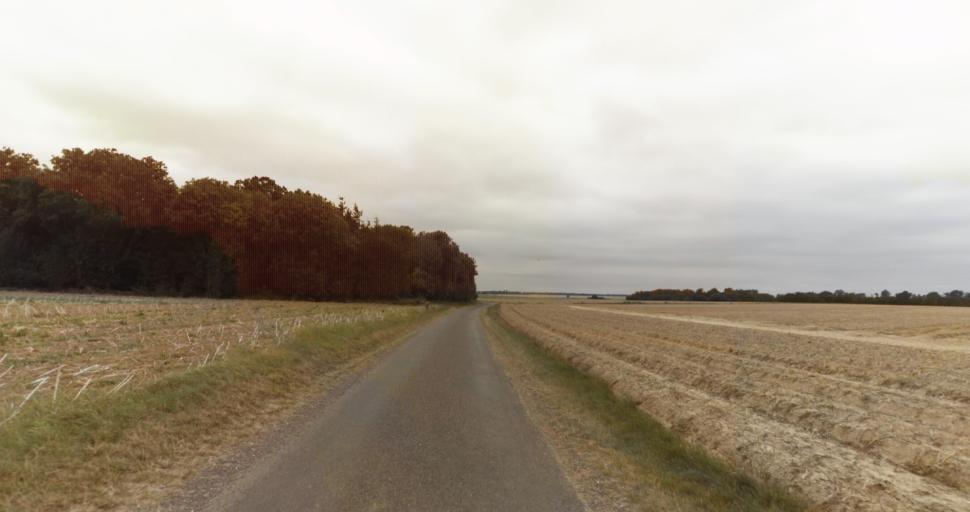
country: FR
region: Haute-Normandie
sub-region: Departement de l'Eure
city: La Couture-Boussey
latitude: 48.9254
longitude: 1.3614
